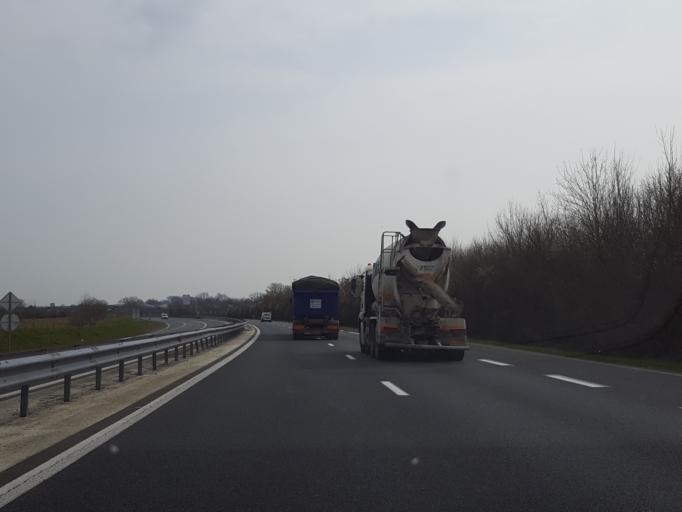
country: FR
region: Pays de la Loire
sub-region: Departement de la Vendee
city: La Ferriere
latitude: 46.6670
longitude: -1.3507
